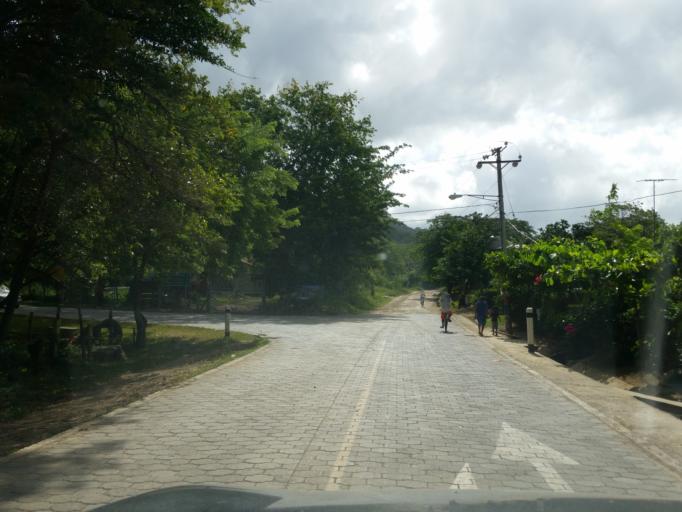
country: NI
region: Rivas
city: San Juan del Sur
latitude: 11.2445
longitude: -85.8454
